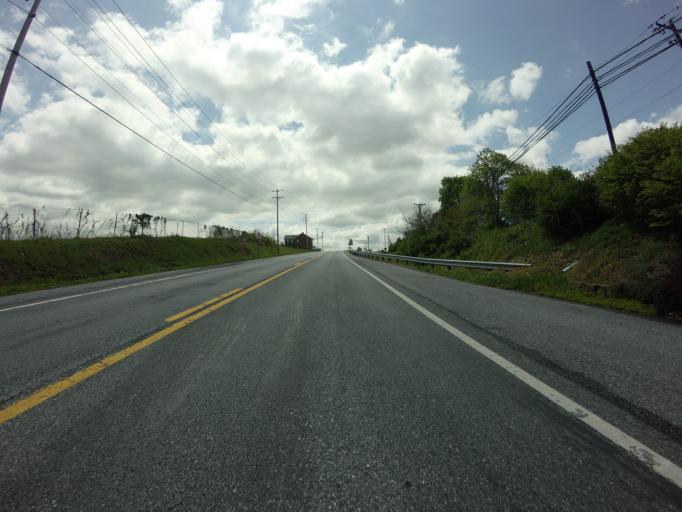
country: US
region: Maryland
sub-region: Frederick County
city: Emmitsburg
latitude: 39.6905
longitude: -77.3329
